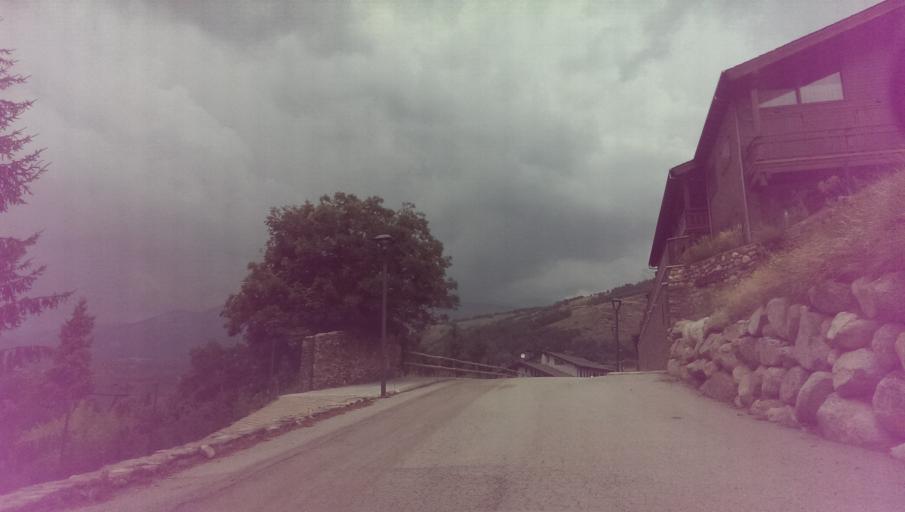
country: ES
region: Catalonia
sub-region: Provincia de Girona
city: Llivia
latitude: 42.4662
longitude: 1.9820
